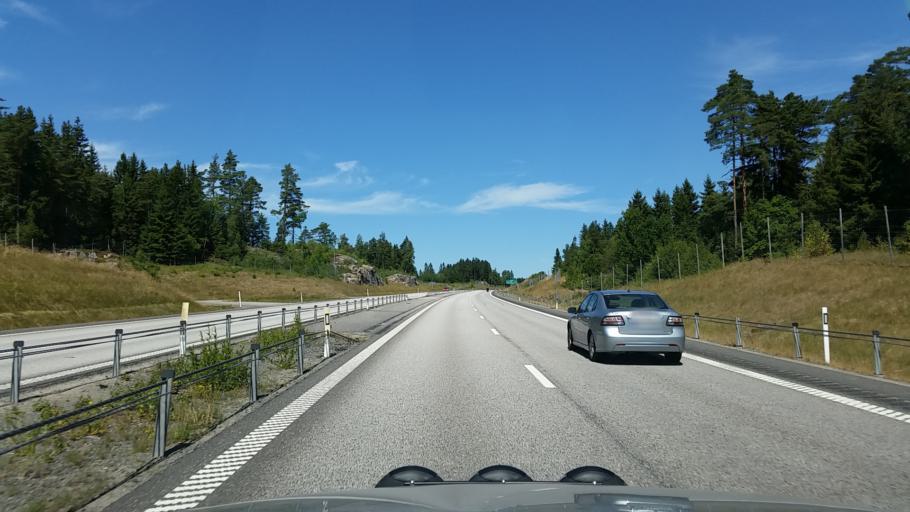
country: SE
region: Vaestra Goetaland
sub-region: Lilla Edets Kommun
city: Lodose
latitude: 58.0455
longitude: 12.1734
